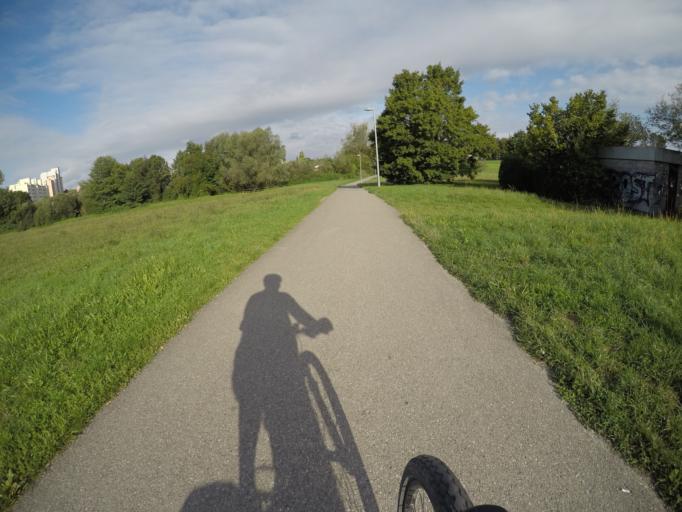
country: DE
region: Baden-Wuerttemberg
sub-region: Regierungsbezirk Stuttgart
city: Magstadt
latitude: 48.7245
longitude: 8.9908
